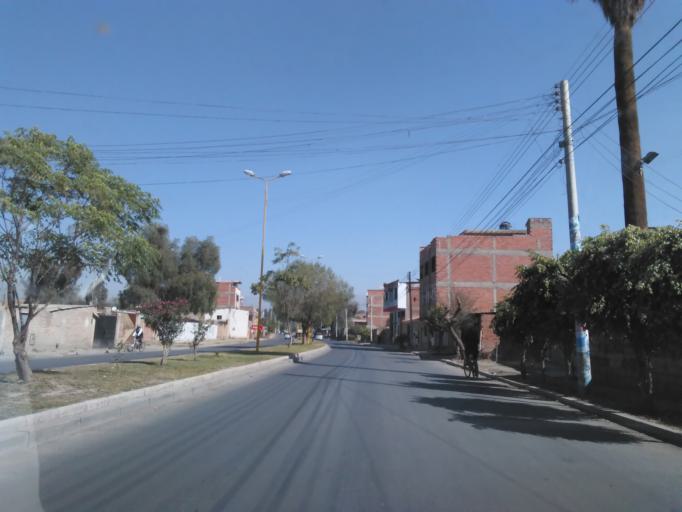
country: BO
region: Cochabamba
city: Cochabamba
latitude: -17.3932
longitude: -66.2627
